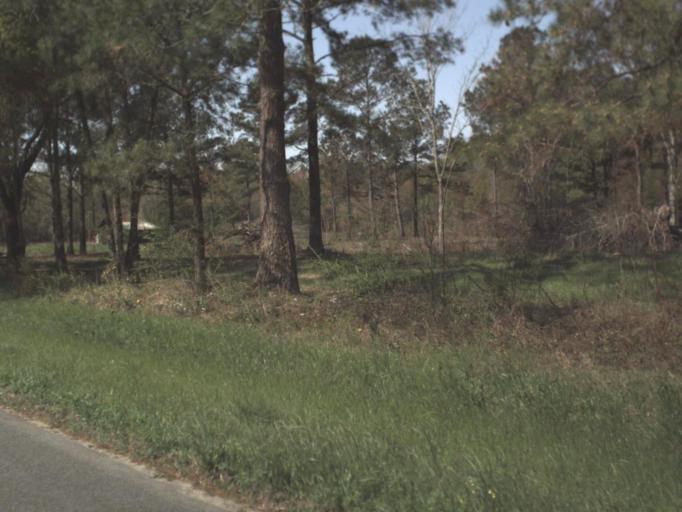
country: US
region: Florida
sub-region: Jackson County
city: Graceville
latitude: 30.8907
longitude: -85.4661
